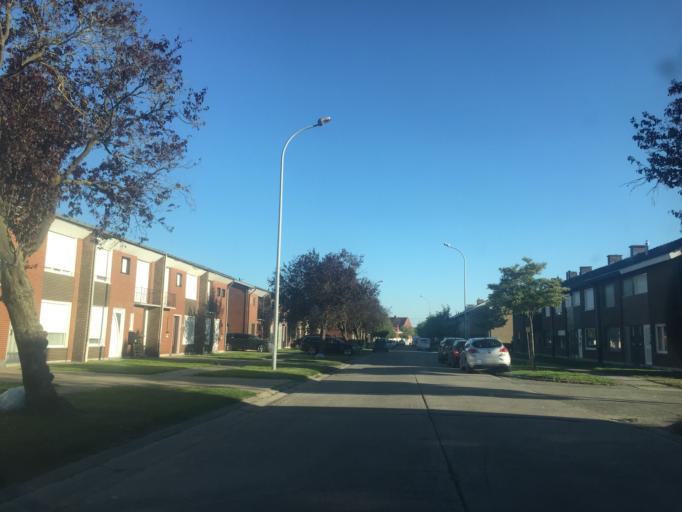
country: BE
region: Flanders
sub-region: Provincie West-Vlaanderen
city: Izegem
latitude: 50.9214
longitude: 3.1957
